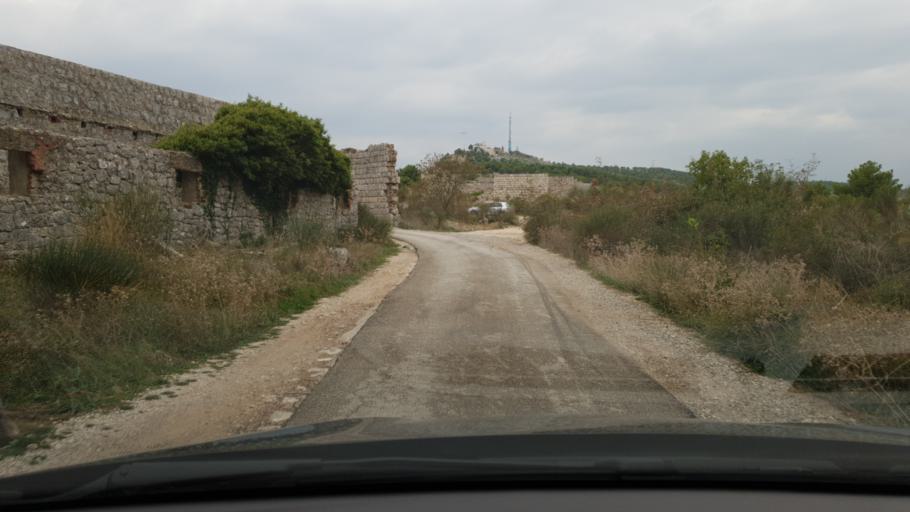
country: HR
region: Dubrovacko-Neretvanska
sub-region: Grad Dubrovnik
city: Dubrovnik
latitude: 42.6441
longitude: 18.1243
